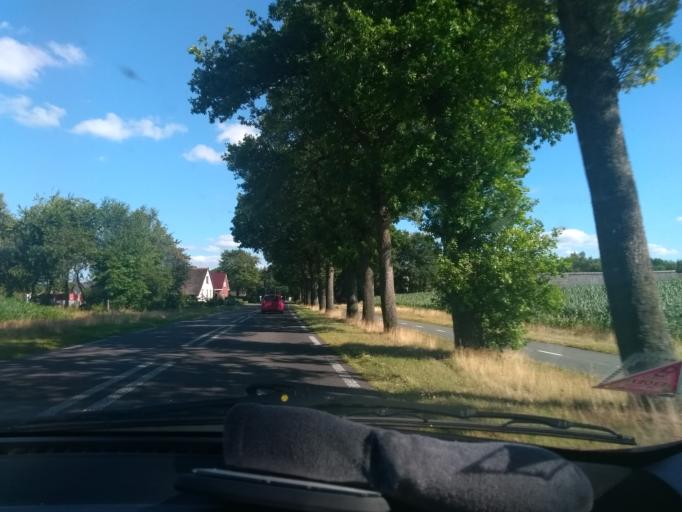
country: NL
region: Drenthe
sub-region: Gemeente Tynaarlo
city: Vries
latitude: 53.0847
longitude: 6.5663
